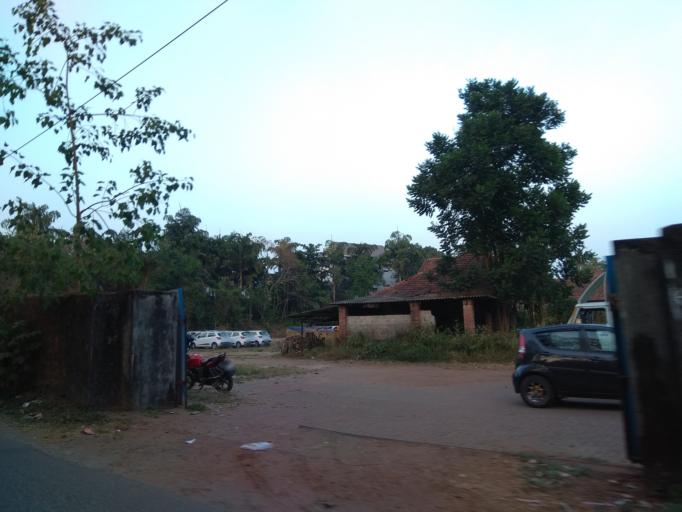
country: IN
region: Karnataka
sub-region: Dakshina Kannada
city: Mangalore
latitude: 12.9260
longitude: 74.8678
